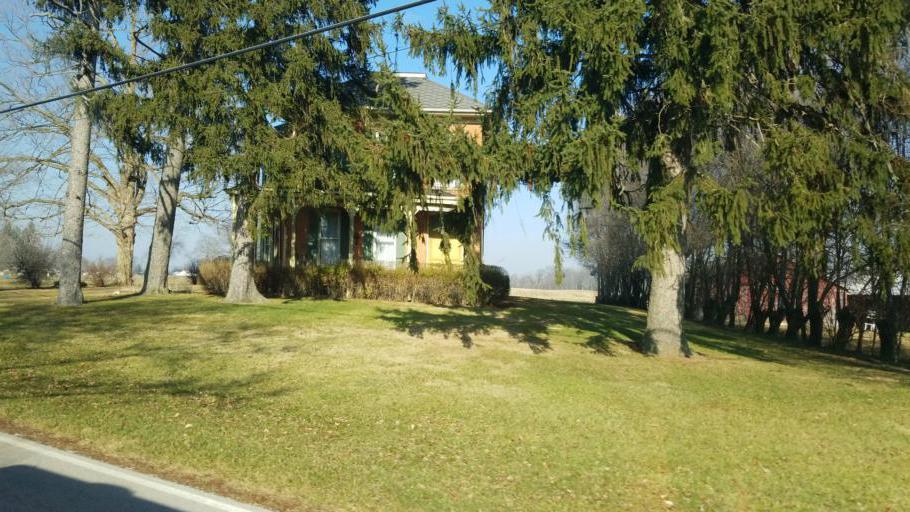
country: US
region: Ohio
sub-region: Seneca County
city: Tiffin
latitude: 41.0994
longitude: -83.1455
